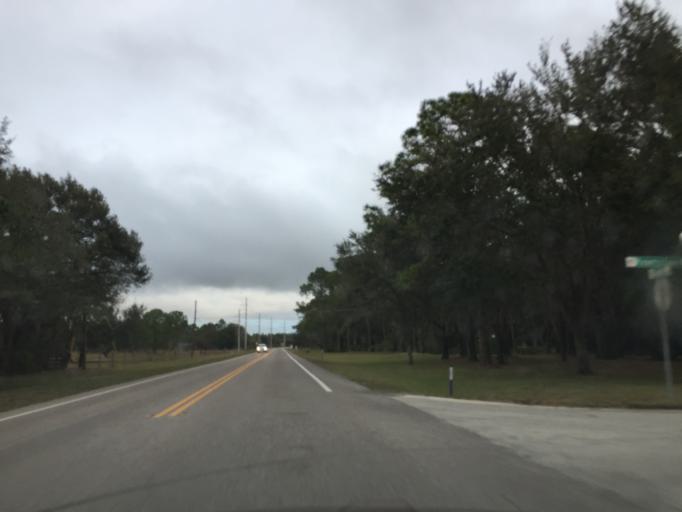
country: US
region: Florida
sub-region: Seminole County
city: Chuluota
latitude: 28.6095
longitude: -81.1279
